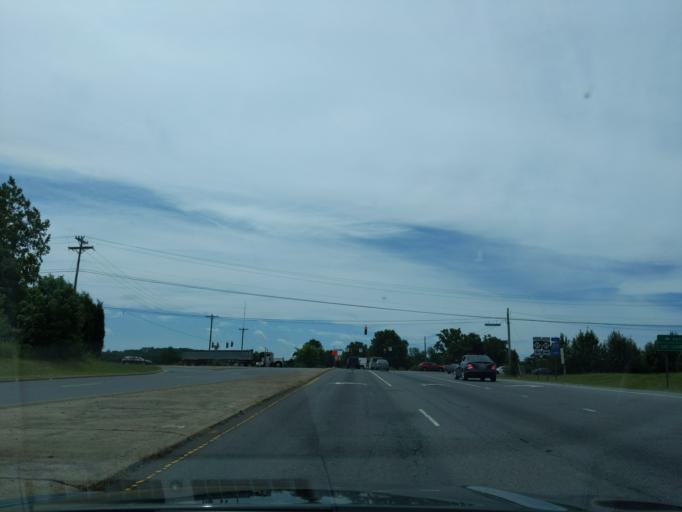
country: US
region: North Carolina
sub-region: Cabarrus County
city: Harrisburg
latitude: 35.3127
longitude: -80.7110
